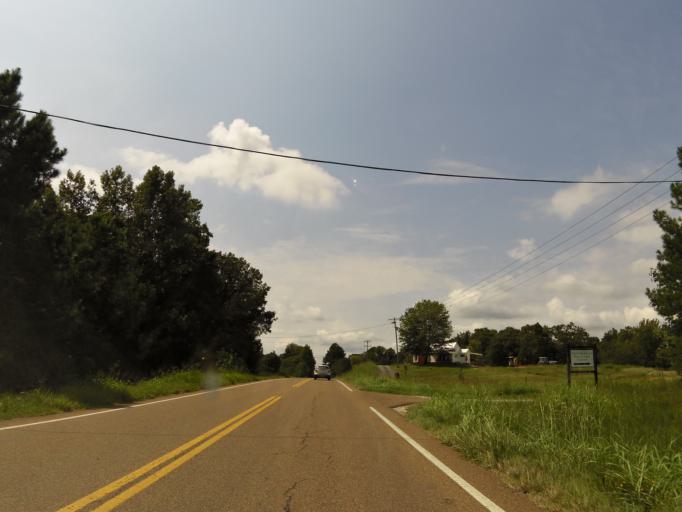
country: US
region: Tennessee
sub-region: Decatur County
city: Decaturville
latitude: 35.5536
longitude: -88.1701
